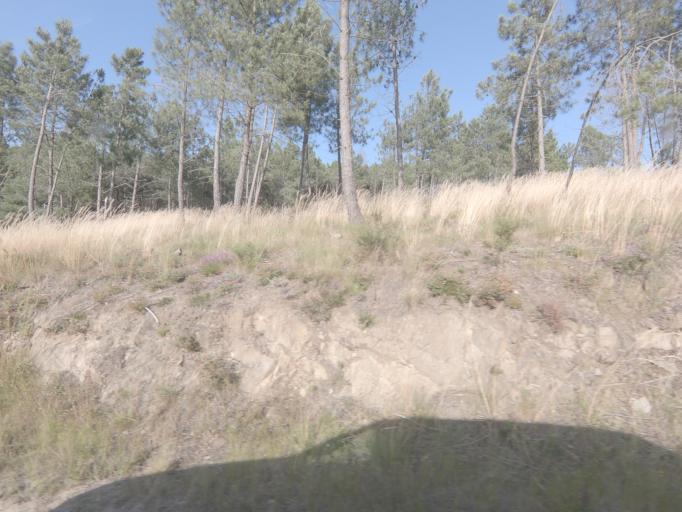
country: PT
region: Vila Real
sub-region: Sabrosa
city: Vilela
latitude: 41.2307
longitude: -7.6068
